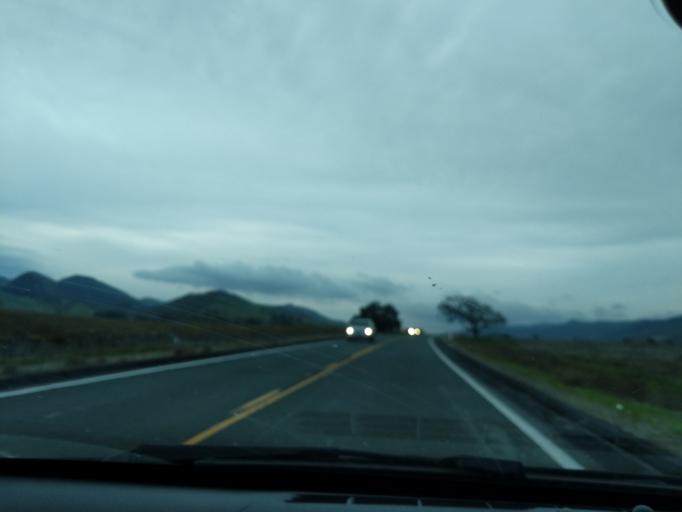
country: US
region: California
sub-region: San Benito County
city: Ridgemark
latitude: 36.6740
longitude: -121.2534
